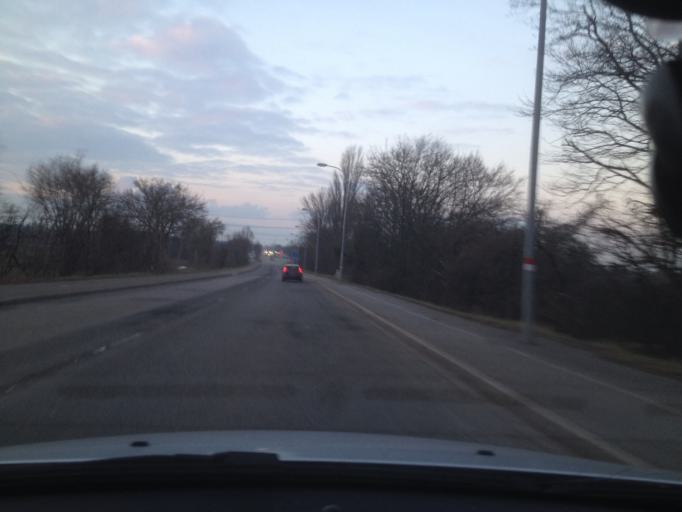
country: DE
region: Baden-Wuerttemberg
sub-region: Karlsruhe Region
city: Ettlingen
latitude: 48.9546
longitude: 8.4066
